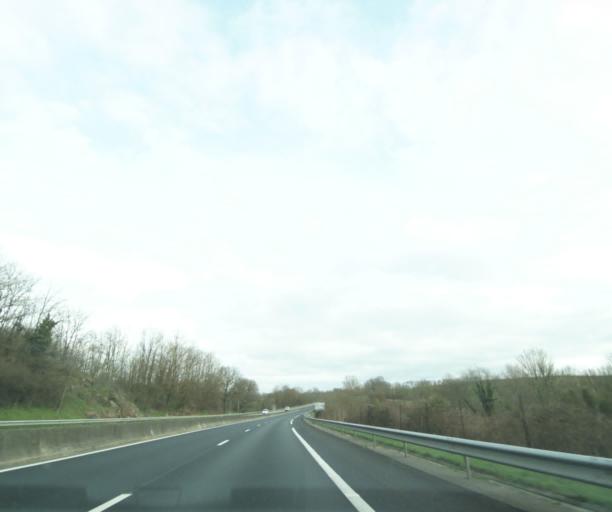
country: FR
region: Limousin
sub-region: Departement de la Haute-Vienne
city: Pierre-Buffiere
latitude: 45.7245
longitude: 1.3468
